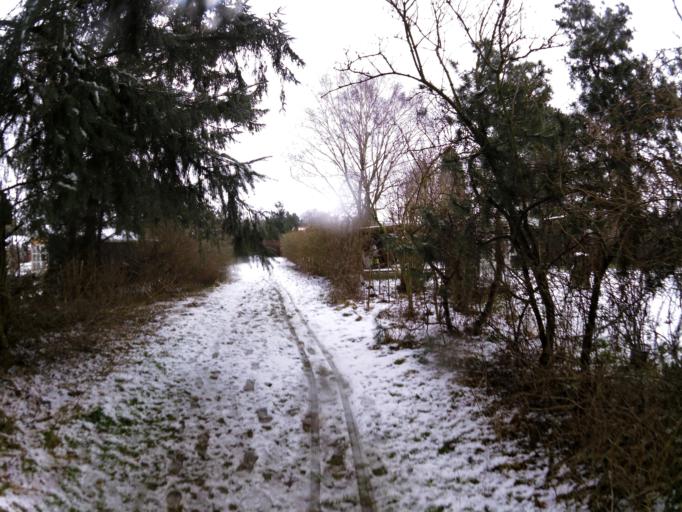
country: DK
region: Zealand
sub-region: Vordingborg Kommune
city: Neder Vindinge
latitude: 55.0538
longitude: 11.8314
